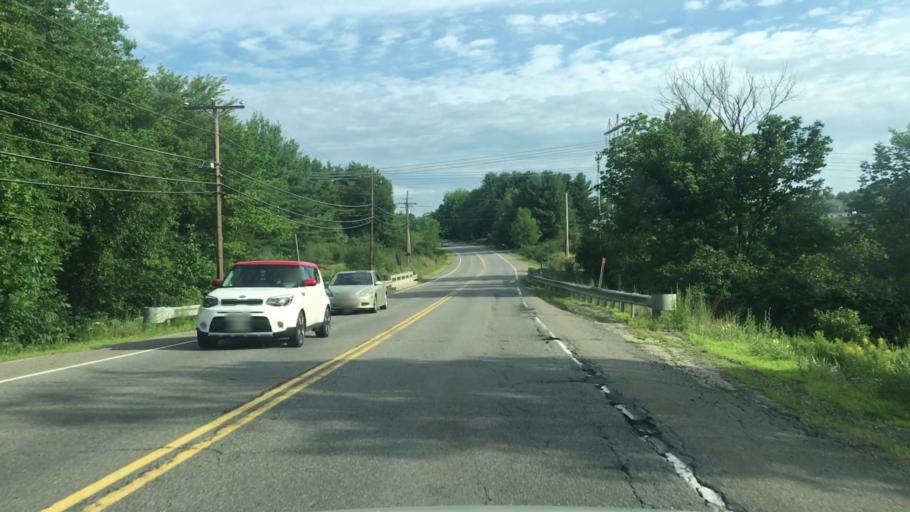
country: US
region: Maine
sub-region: Cumberland County
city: Gorham
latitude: 43.6432
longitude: -70.4215
